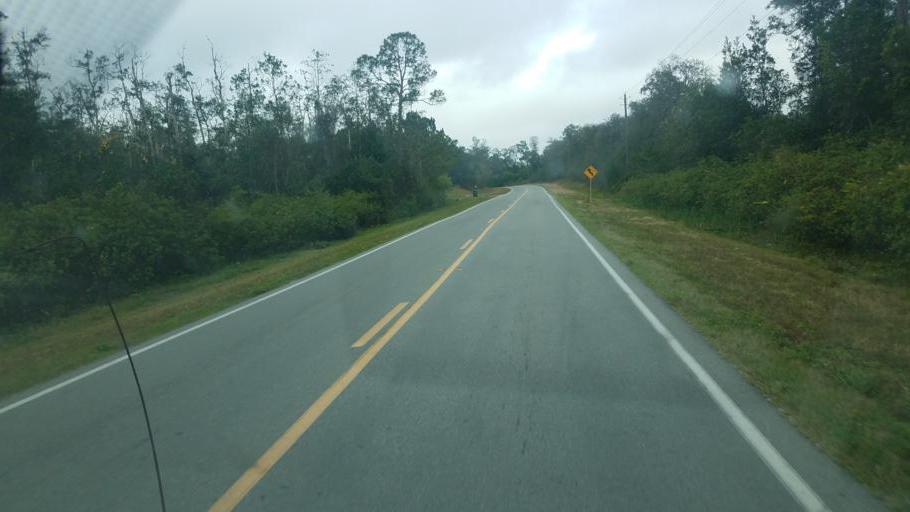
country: US
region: Florida
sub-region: Polk County
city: Polk City
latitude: 28.2586
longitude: -81.8003
